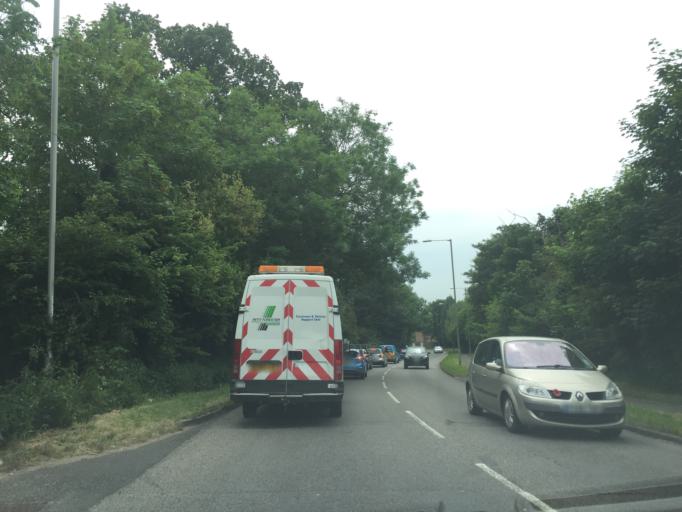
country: GB
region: England
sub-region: Dorset
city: Ferndown
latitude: 50.7899
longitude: -1.9046
